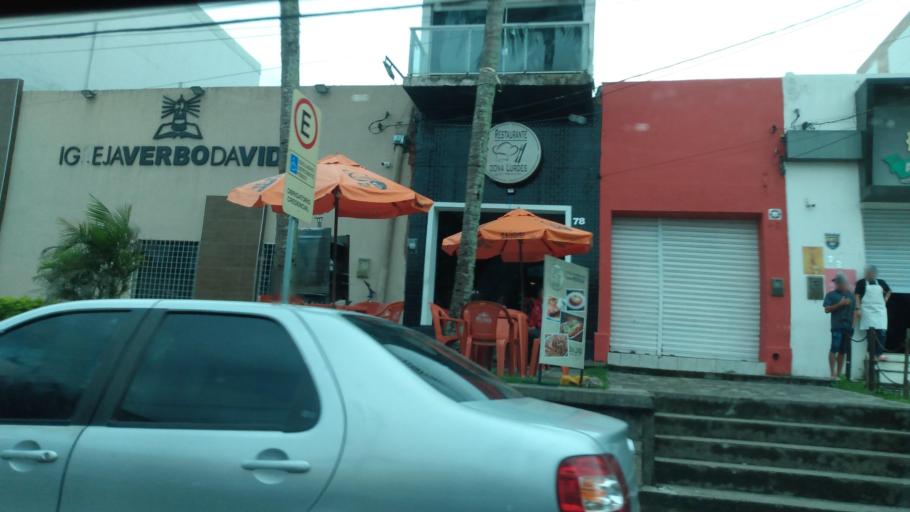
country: BR
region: Pernambuco
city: Garanhuns
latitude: -8.8892
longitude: -36.4946
